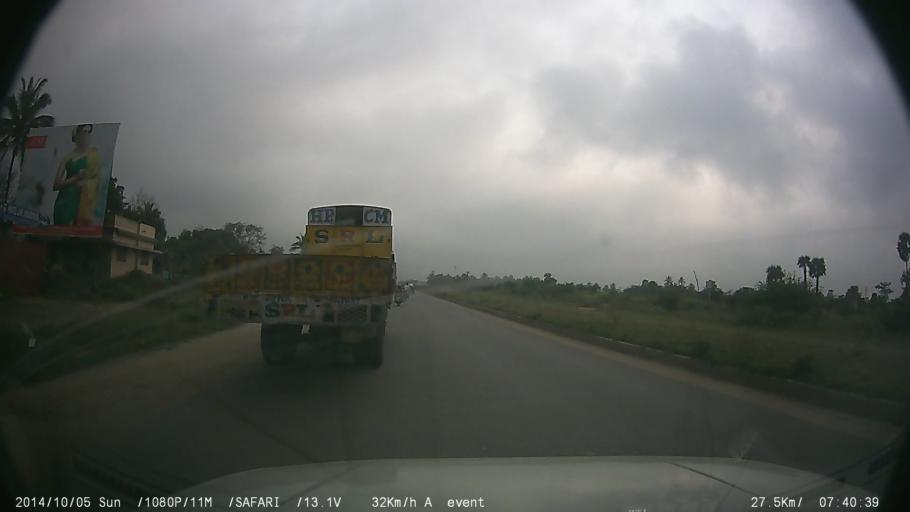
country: IN
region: Tamil Nadu
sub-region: Coimbatore
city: Madukkarai
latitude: 10.8864
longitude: 76.9145
